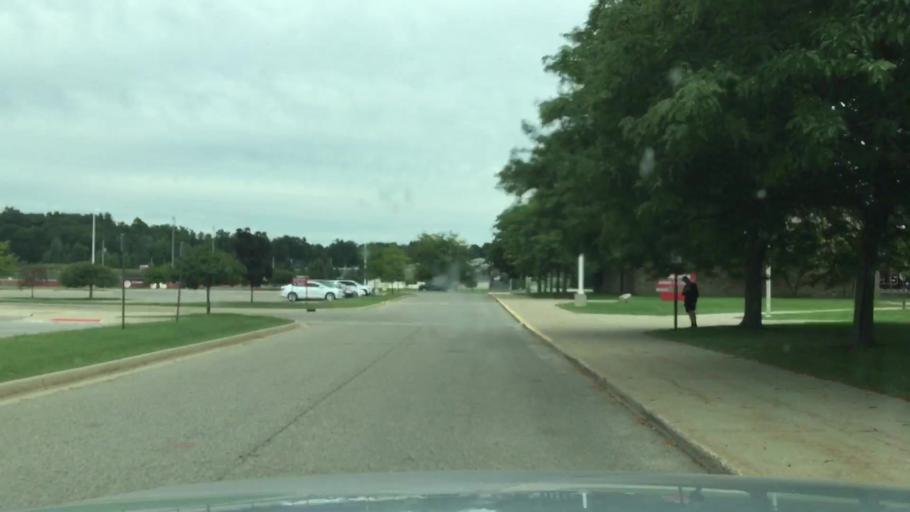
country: US
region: Michigan
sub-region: Genesee County
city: Linden
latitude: 42.8090
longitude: -83.8143
